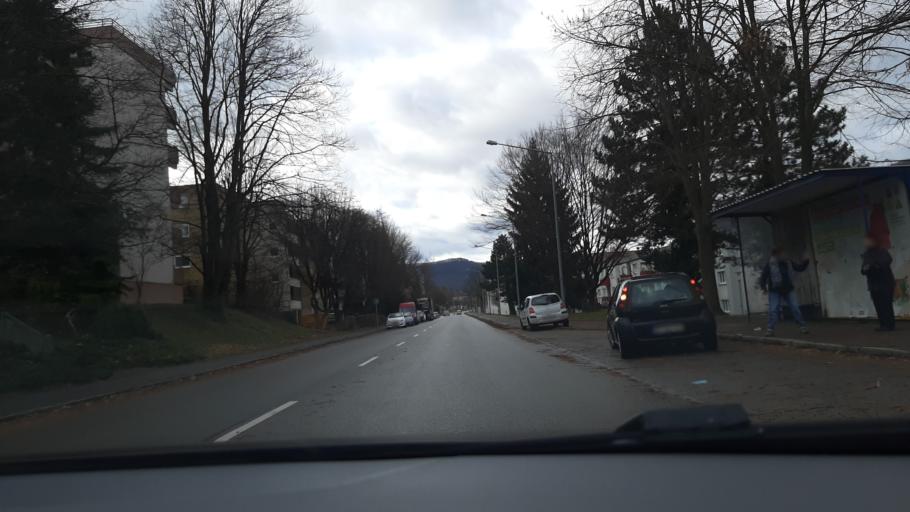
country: DE
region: Baden-Wuerttemberg
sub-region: Regierungsbezirk Stuttgart
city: Geislingen an der Steige
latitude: 48.6191
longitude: 9.8198
